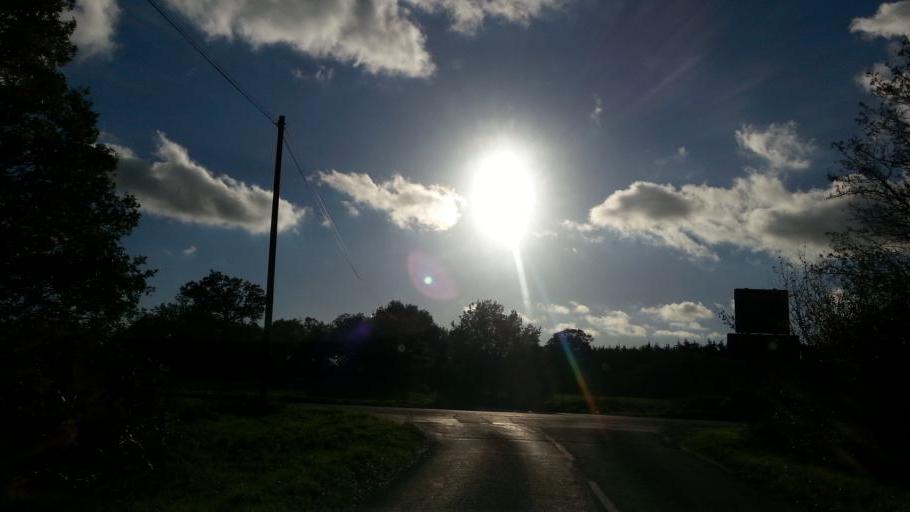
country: GB
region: England
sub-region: Suffolk
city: Thurston
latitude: 52.2333
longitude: 0.8056
